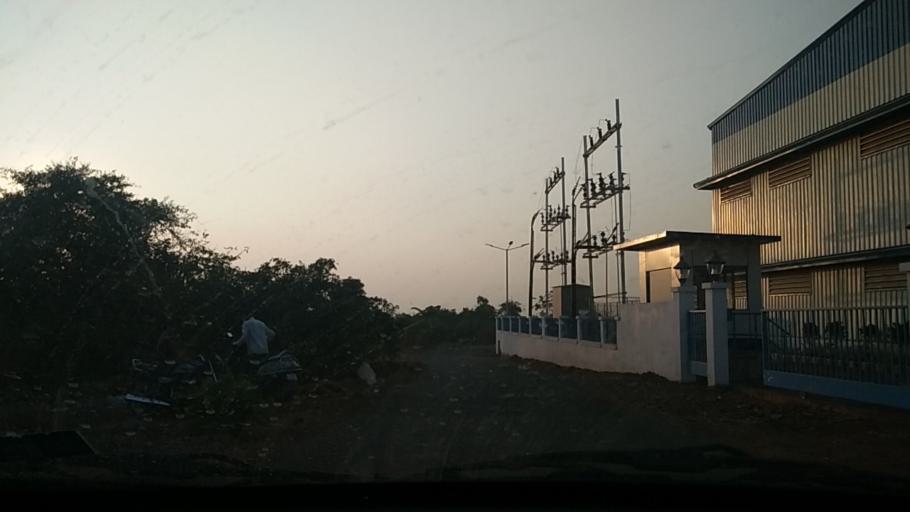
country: IN
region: Goa
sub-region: South Goa
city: Raia
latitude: 15.3454
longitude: 73.9537
